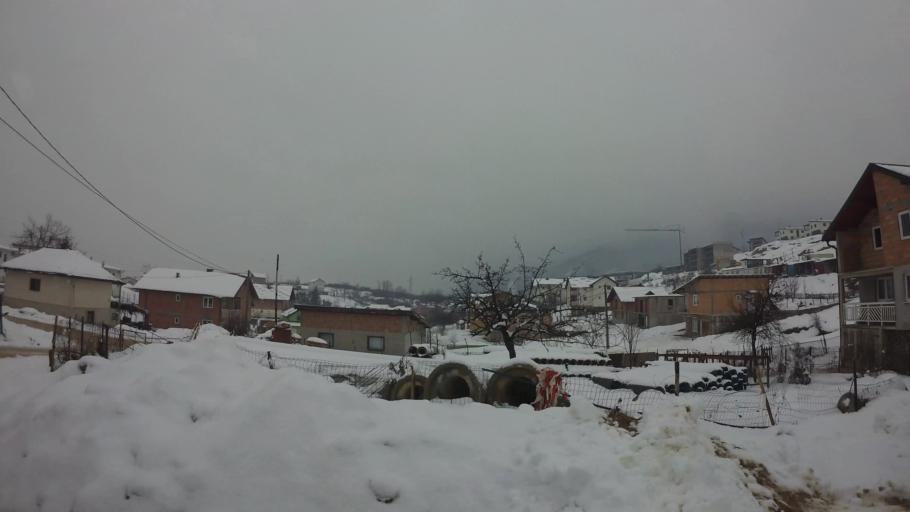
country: BA
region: Federation of Bosnia and Herzegovina
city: Hadzici
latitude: 43.8437
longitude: 18.2633
